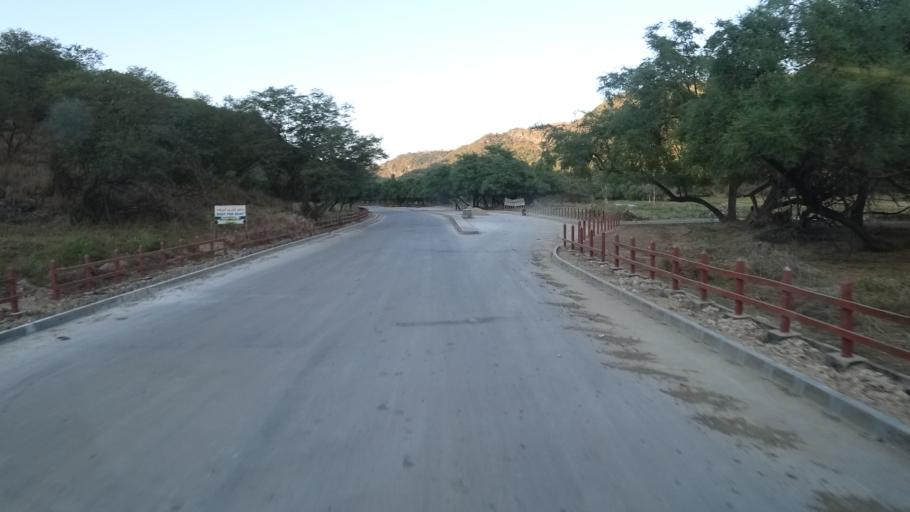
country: OM
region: Zufar
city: Salalah
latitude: 17.0967
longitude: 54.4495
